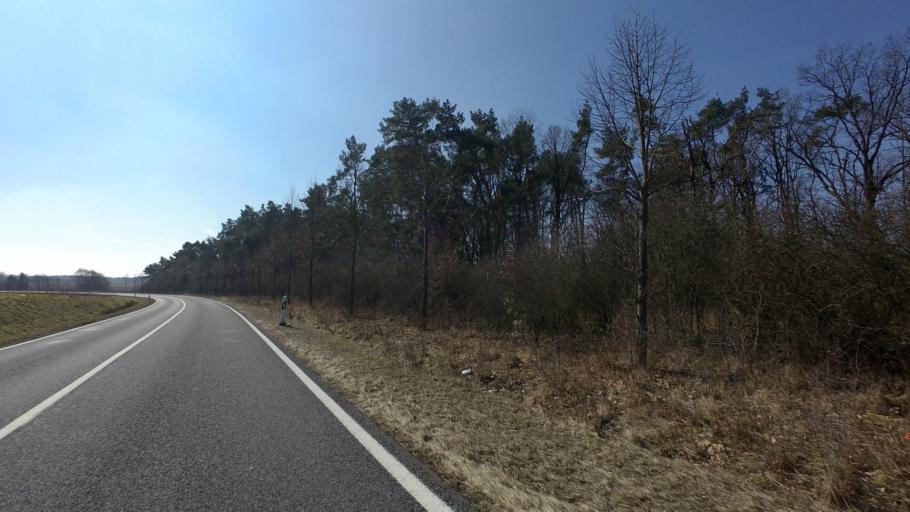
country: DE
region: Saxony-Anhalt
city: Nudersdorf
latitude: 51.9603
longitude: 12.5880
